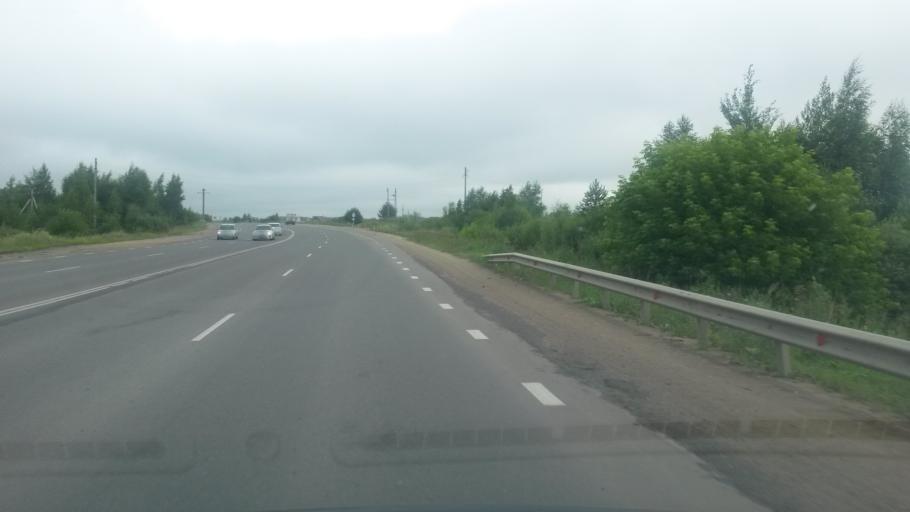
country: RU
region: Ivanovo
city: Novo-Talitsy
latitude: 57.0139
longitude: 40.8838
